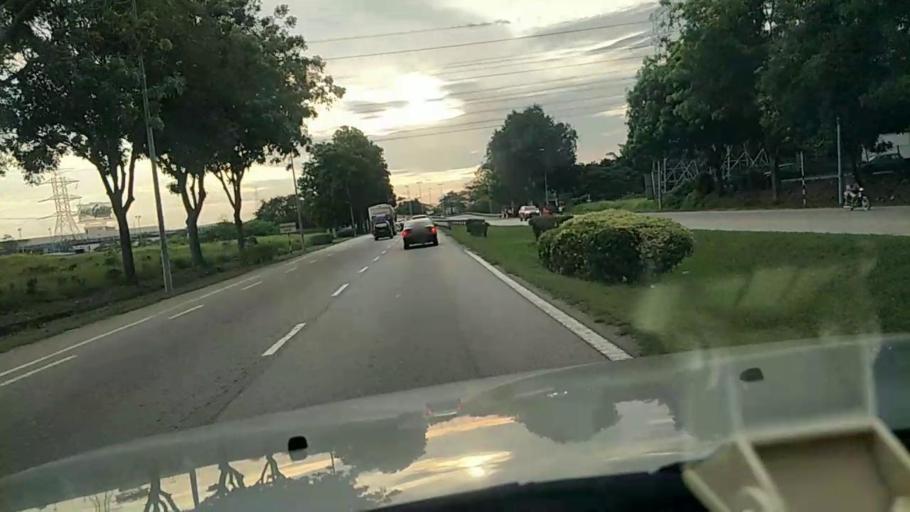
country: MY
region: Selangor
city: Klang
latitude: 3.1090
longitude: 101.4462
